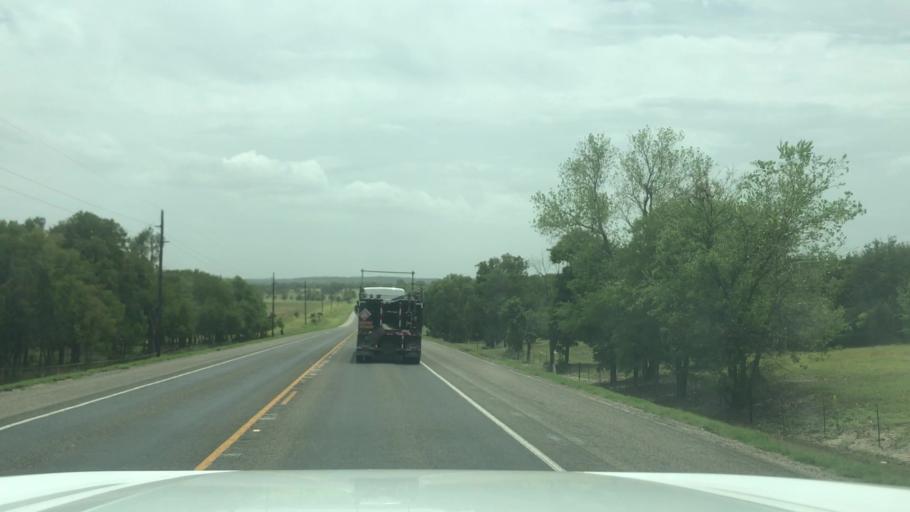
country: US
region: Texas
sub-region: Bosque County
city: Clifton
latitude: 31.7171
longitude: -97.5474
